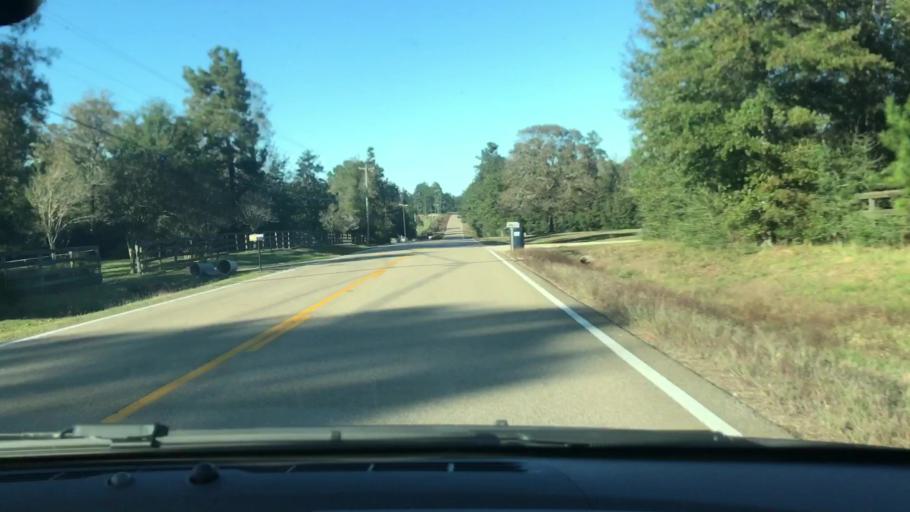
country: US
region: Louisiana
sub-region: Saint Tammany Parish
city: Abita Springs
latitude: 30.6307
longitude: -90.0163
